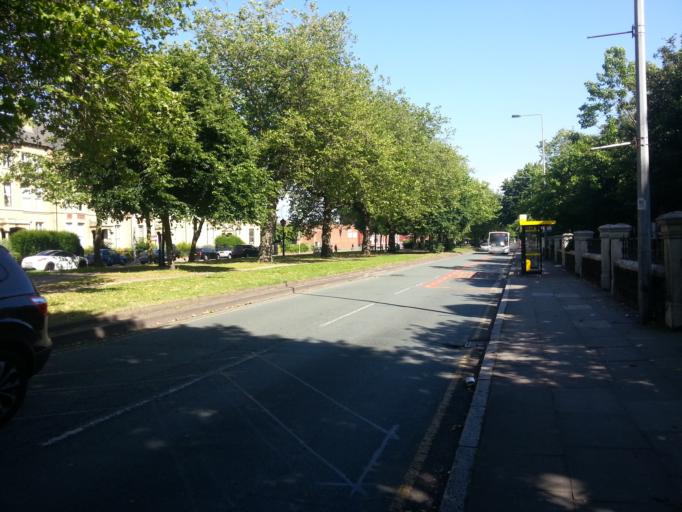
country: GB
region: England
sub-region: Liverpool
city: Liverpool
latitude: 53.3932
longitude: -2.9616
